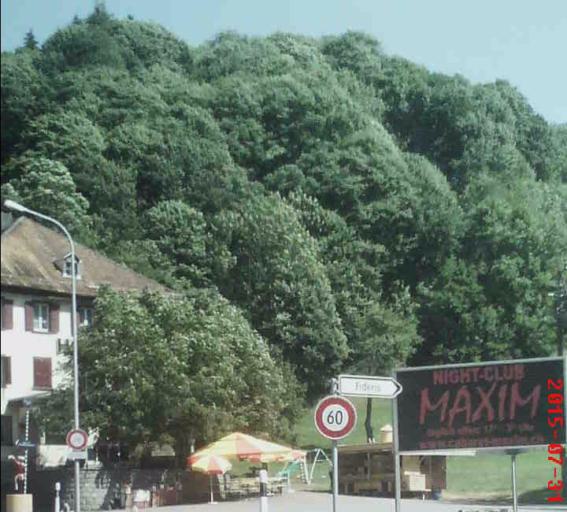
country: CH
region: Grisons
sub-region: Praettigau/Davos District
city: Jenaz
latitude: 46.9225
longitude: 9.7317
